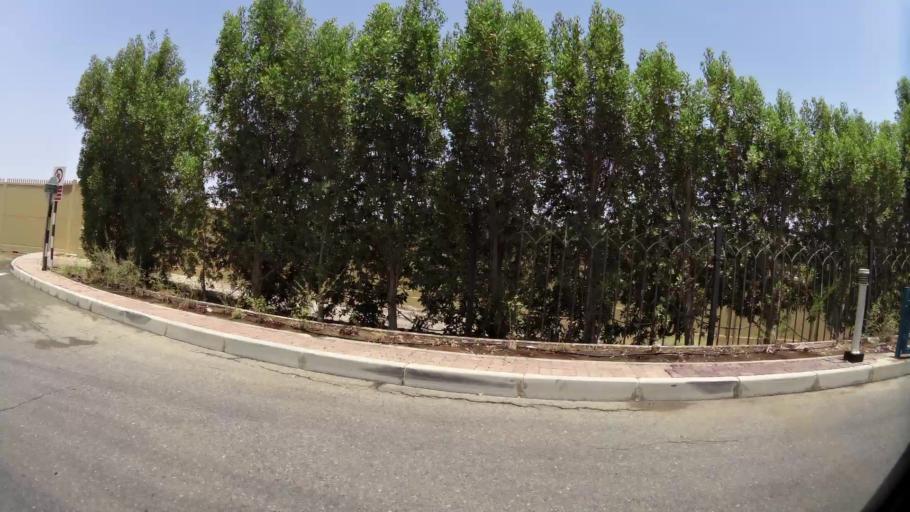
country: OM
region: Muhafazat Masqat
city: Bawshar
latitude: 23.6037
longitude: 58.4781
